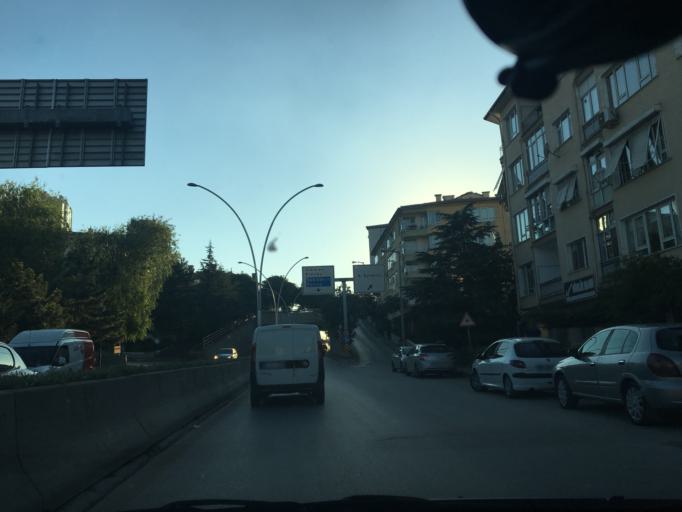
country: TR
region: Ankara
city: Ankara
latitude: 39.8955
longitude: 32.8494
